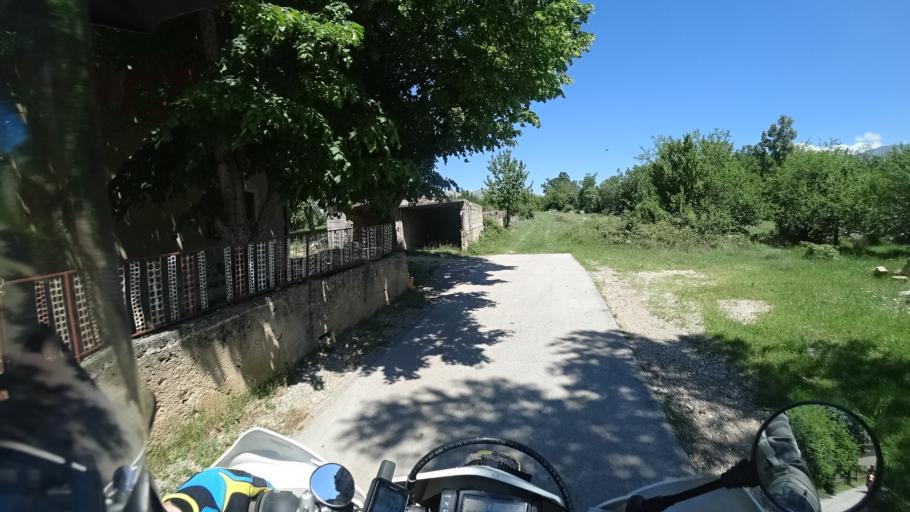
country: BA
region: Federation of Bosnia and Herzegovina
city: Bosansko Grahovo
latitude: 43.9776
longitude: 16.4247
